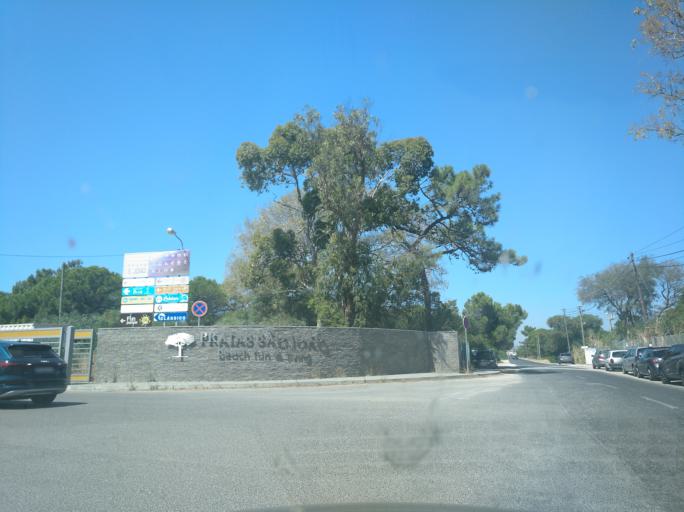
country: PT
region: Setubal
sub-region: Almada
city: Trafaria
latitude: 38.6616
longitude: -9.2435
